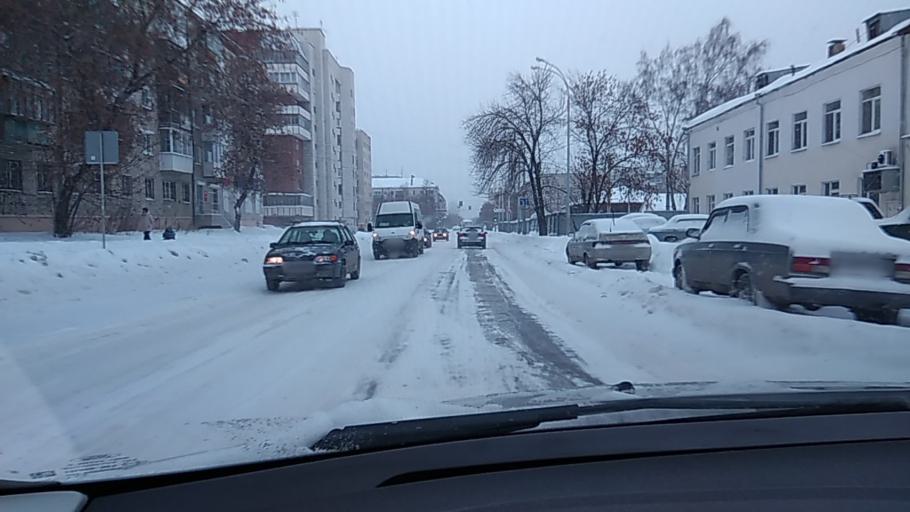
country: RU
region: Sverdlovsk
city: Yekaterinburg
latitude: 56.8120
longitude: 60.6119
